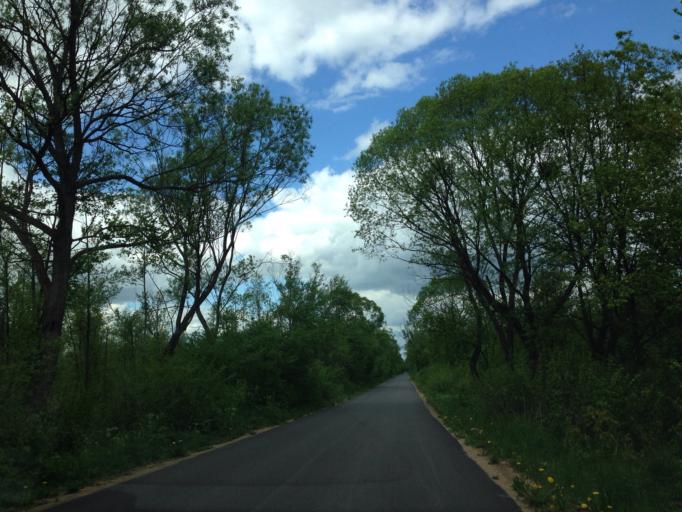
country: PL
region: Podlasie
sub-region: Powiat bialostocki
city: Tykocin
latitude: 53.3198
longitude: 22.6017
